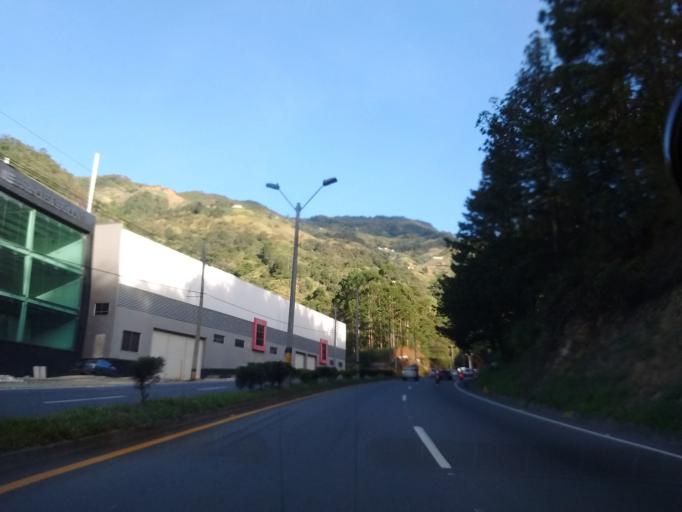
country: CO
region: Antioquia
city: Bello
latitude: 6.3199
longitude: -75.5326
